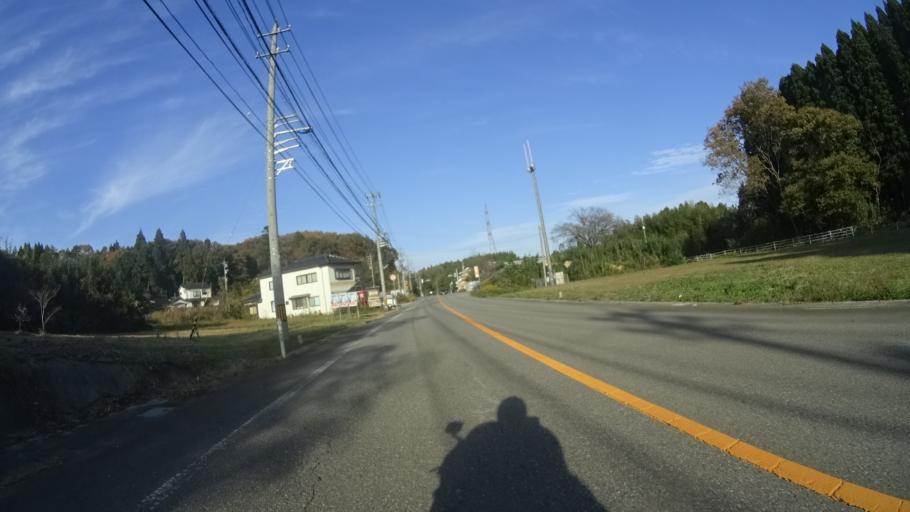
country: JP
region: Ishikawa
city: Hakui
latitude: 37.0571
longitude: 136.7770
